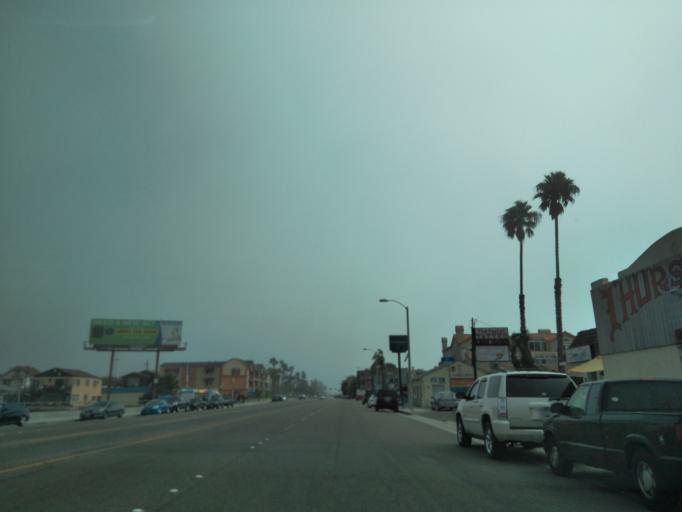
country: US
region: California
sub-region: Orange County
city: Seal Beach
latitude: 33.7172
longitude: -118.0696
